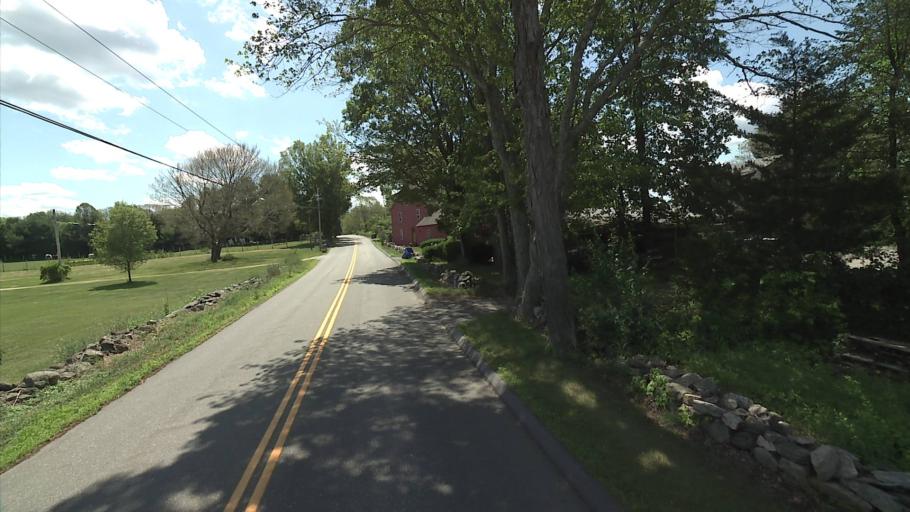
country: US
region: Connecticut
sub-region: New London County
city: Jewett City
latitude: 41.5863
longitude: -71.9017
